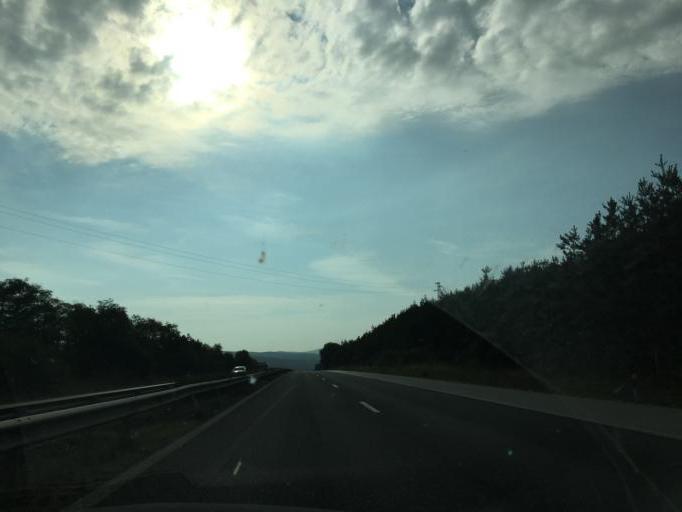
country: BG
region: Sofiya
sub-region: Obshtina Gorna Malina
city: Gorna Malina
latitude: 42.5489
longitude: 23.7056
